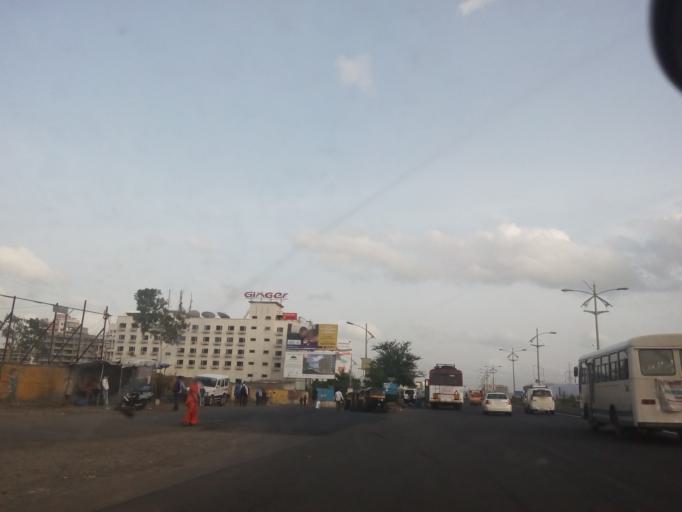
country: IN
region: Maharashtra
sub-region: Pune Division
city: Pimpri
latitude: 18.6078
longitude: 73.7514
